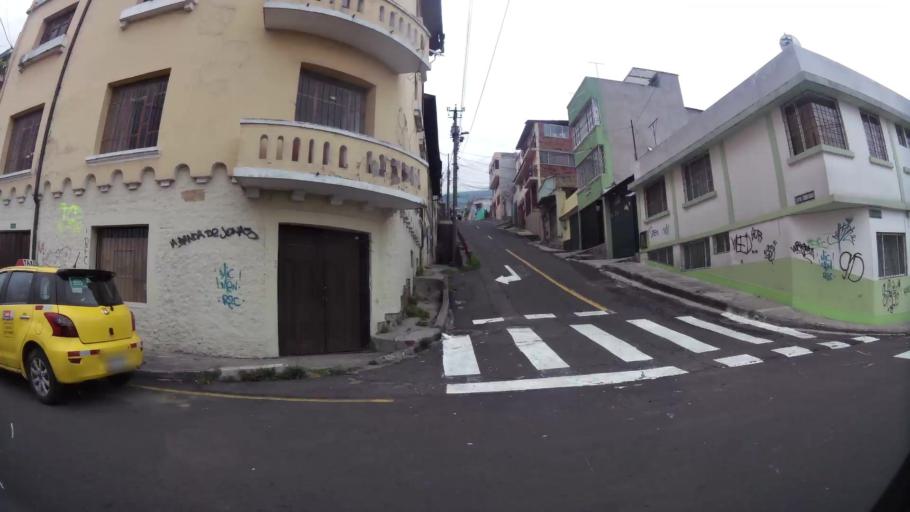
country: EC
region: Pichincha
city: Quito
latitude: -0.2137
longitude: -78.5084
